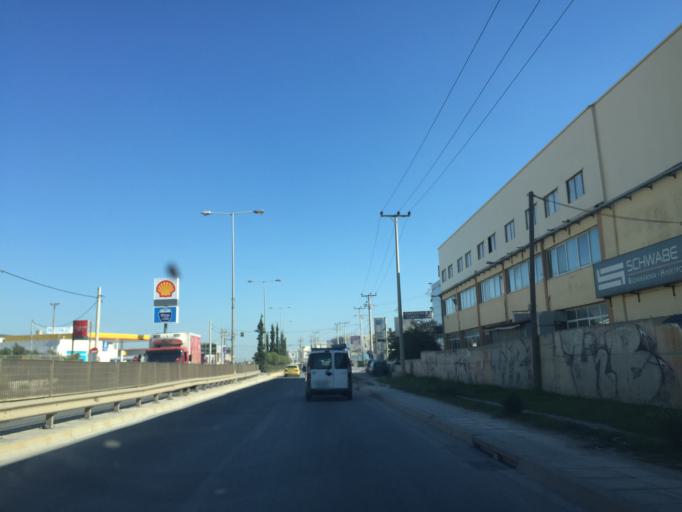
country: GR
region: Attica
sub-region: Nomarchia Anatolikis Attikis
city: Koropi
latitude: 37.8766
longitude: 23.8670
